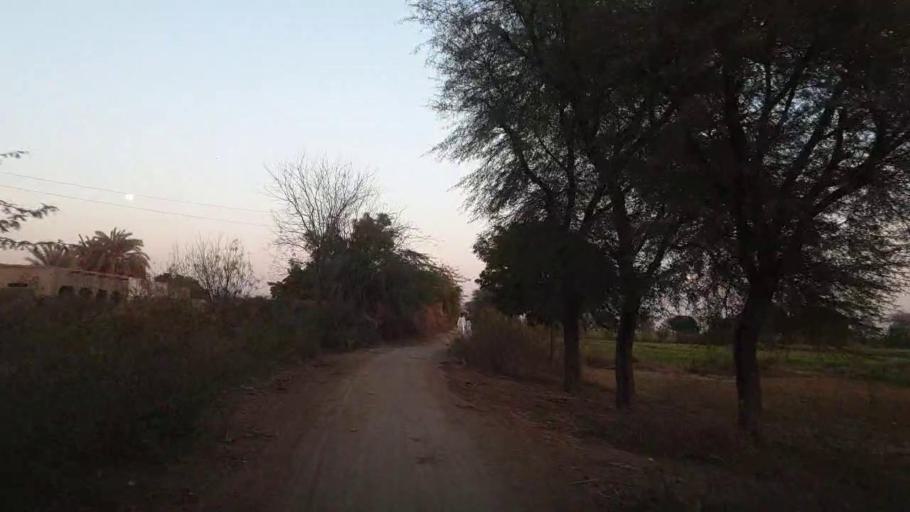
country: PK
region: Sindh
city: Mirpur Khas
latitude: 25.6910
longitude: 69.0544
